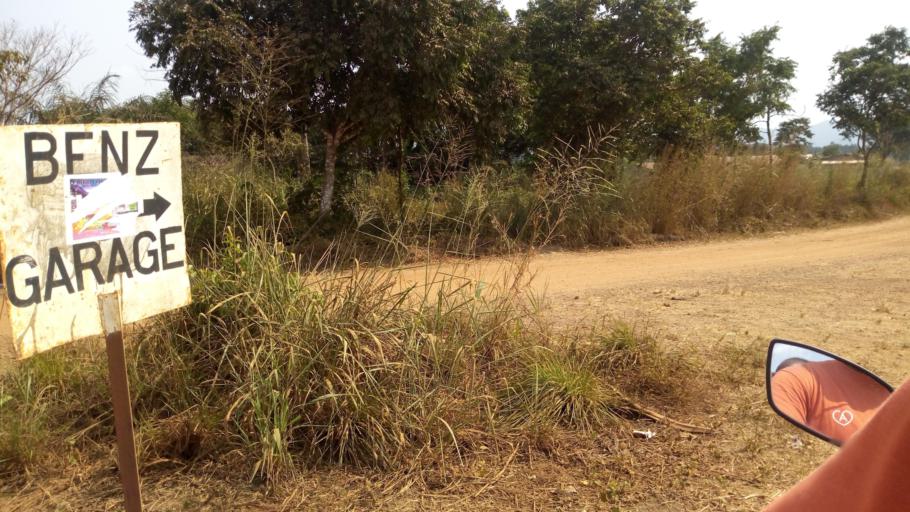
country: SL
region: Southern Province
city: Mogbwemo
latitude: 7.7758
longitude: -12.2997
